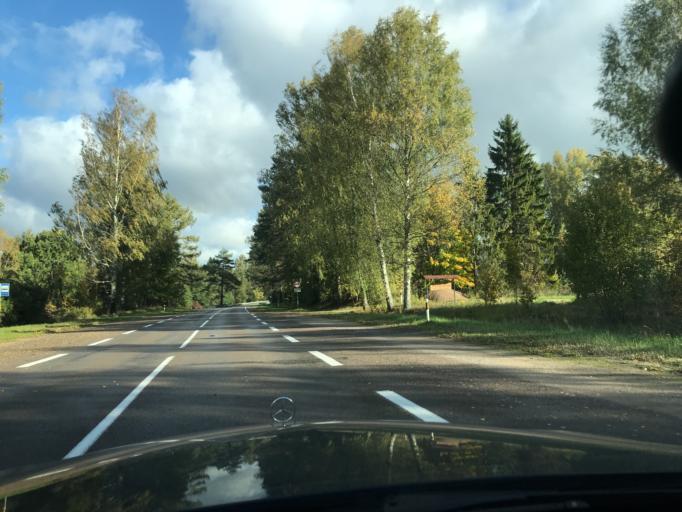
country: EE
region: Valgamaa
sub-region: Torva linn
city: Torva
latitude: 58.0040
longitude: 26.0817
